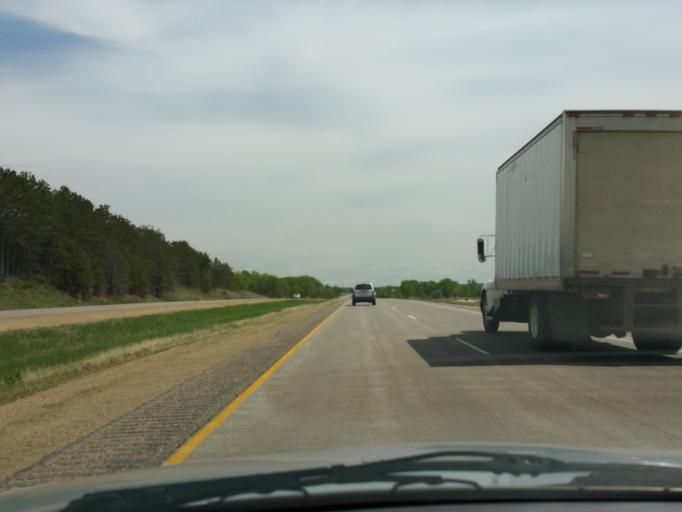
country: US
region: Wisconsin
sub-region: Pierce County
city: River Falls
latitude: 44.9258
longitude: -92.6787
